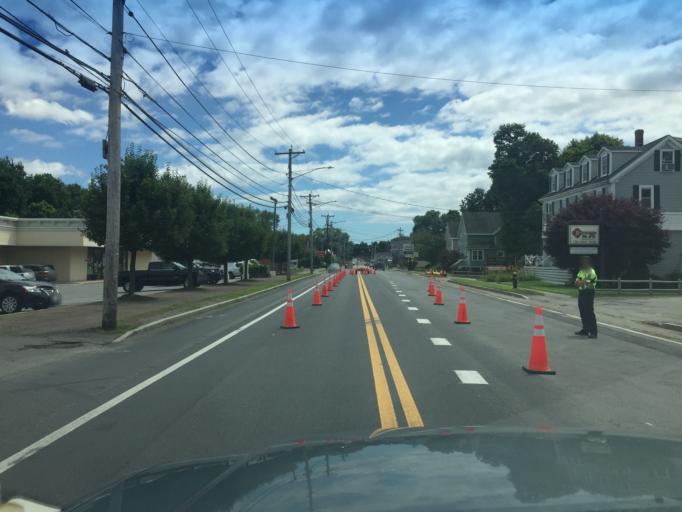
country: US
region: Massachusetts
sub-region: Middlesex County
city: Reading
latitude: 42.5189
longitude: -71.1034
